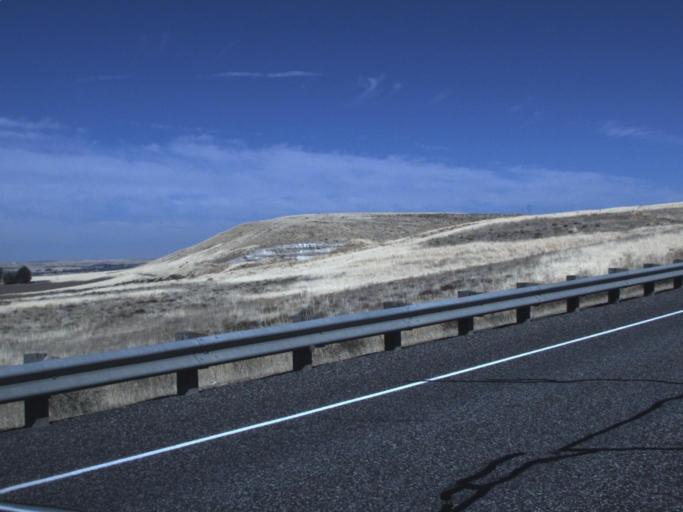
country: US
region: Washington
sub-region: Walla Walla County
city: Burbank
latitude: 46.2678
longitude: -118.7773
